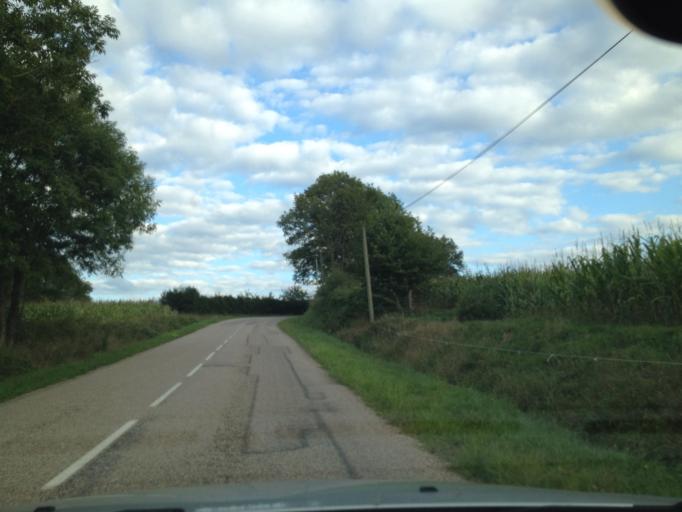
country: FR
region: Lorraine
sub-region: Departement des Vosges
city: Bains-les-Bains
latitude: 47.9761
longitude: 6.1708
